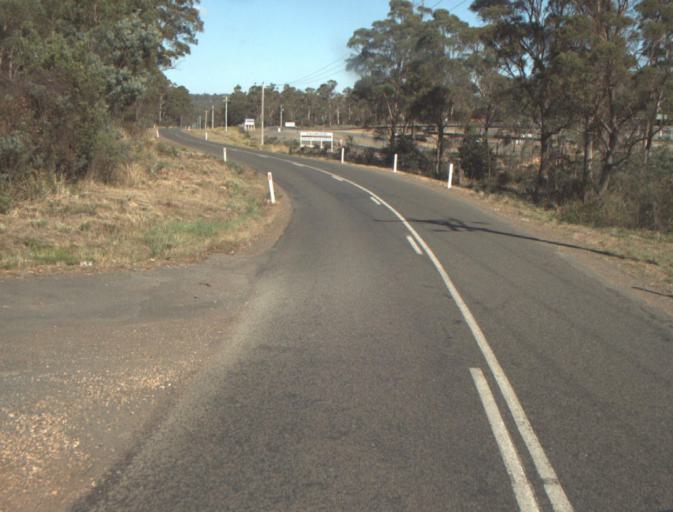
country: AU
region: Tasmania
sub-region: Launceston
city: Mayfield
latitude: -41.3203
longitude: 147.1354
